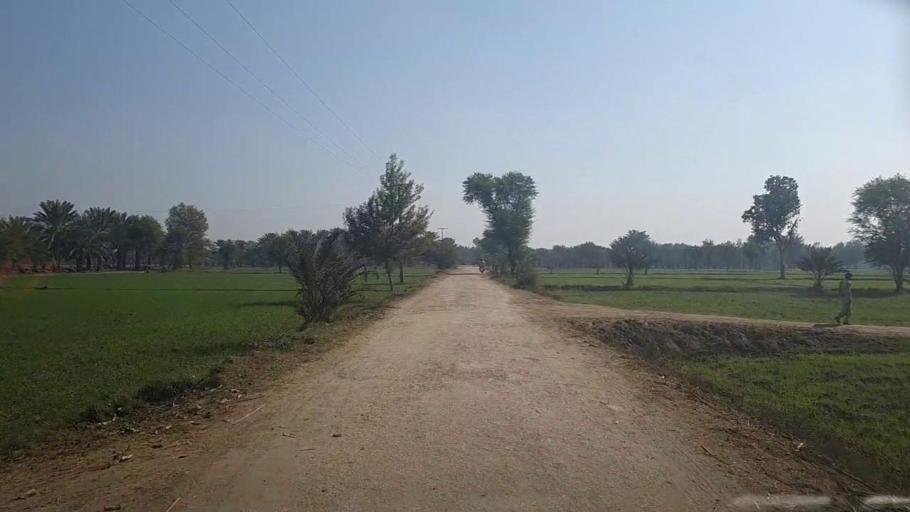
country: PK
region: Sindh
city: Kot Diji
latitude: 27.4346
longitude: 68.7171
